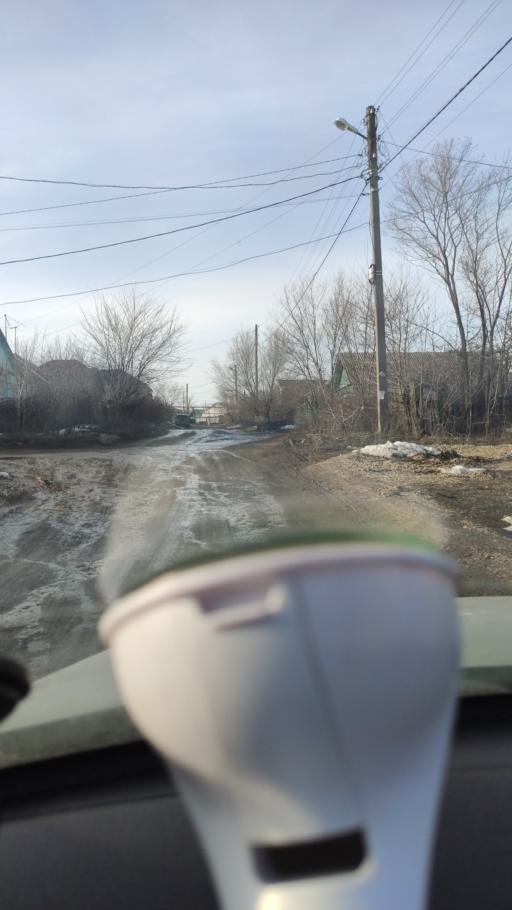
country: RU
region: Samara
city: Smyshlyayevka
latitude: 53.2432
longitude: 50.4881
